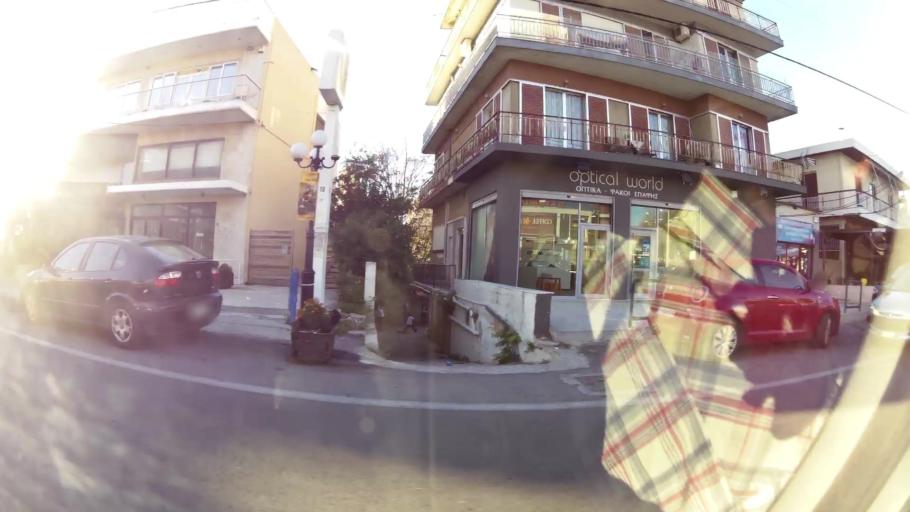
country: GR
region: Attica
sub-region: Nomarchia Athinas
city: Lykovrysi
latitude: 38.0689
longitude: 23.7821
